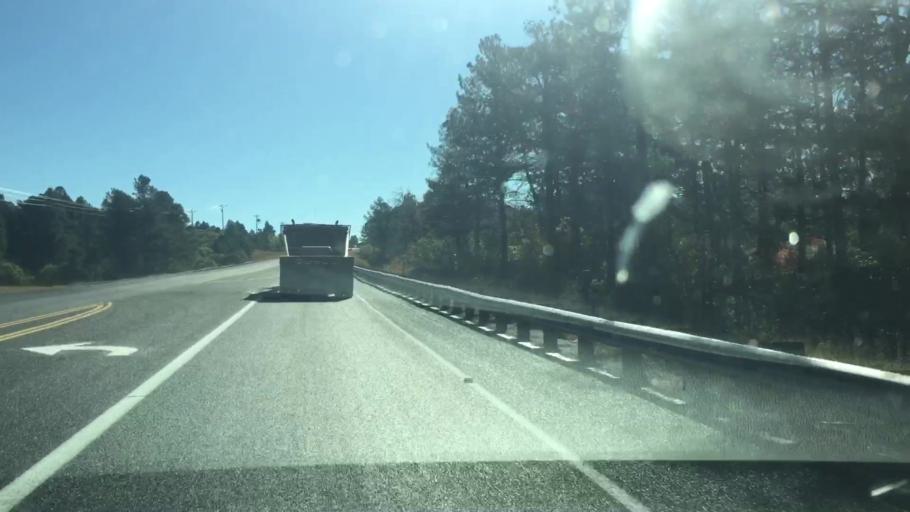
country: US
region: Colorado
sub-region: Elbert County
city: Ponderosa Park
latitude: 39.3765
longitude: -104.6940
